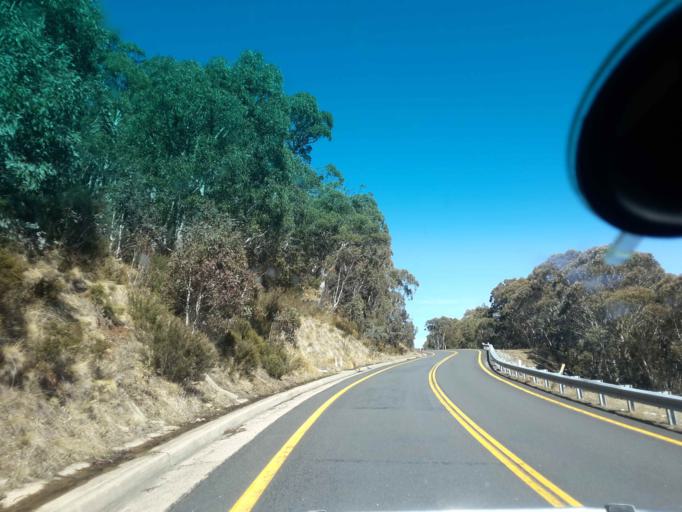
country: AU
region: New South Wales
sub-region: Snowy River
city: Jindabyne
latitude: -36.4908
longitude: 148.3336
